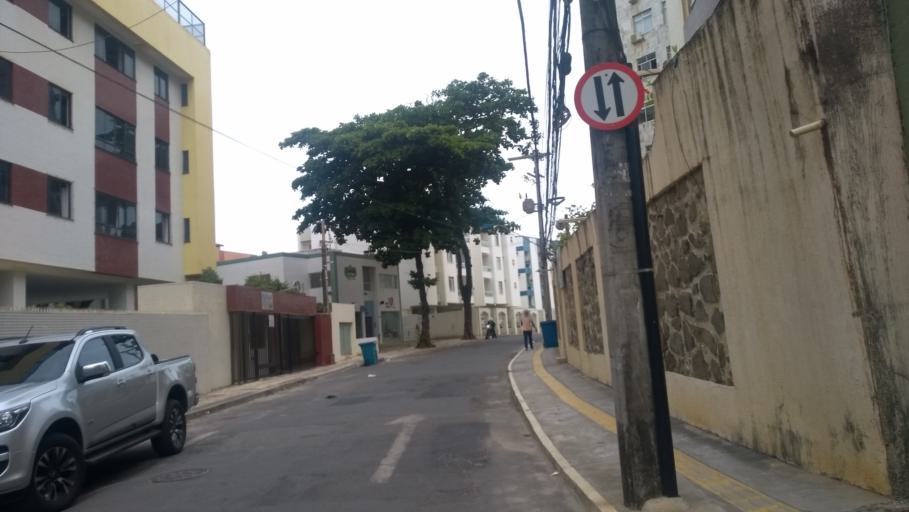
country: BR
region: Bahia
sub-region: Salvador
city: Salvador
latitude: -12.9960
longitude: -38.4459
